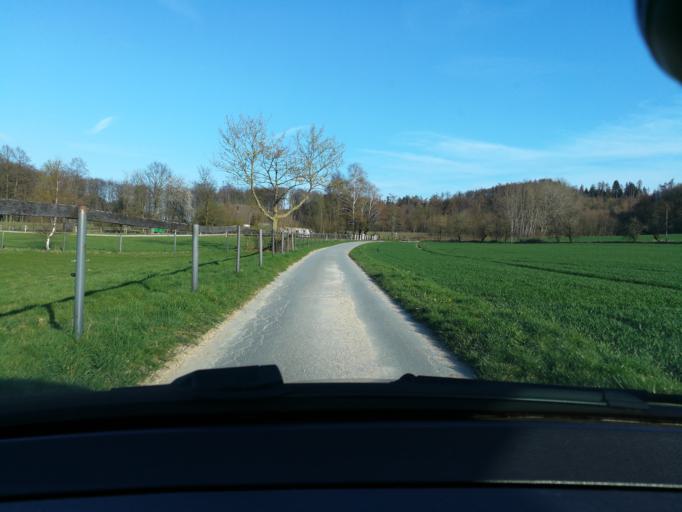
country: DE
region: North Rhine-Westphalia
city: Borgholzhausen
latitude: 52.0902
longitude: 8.3095
